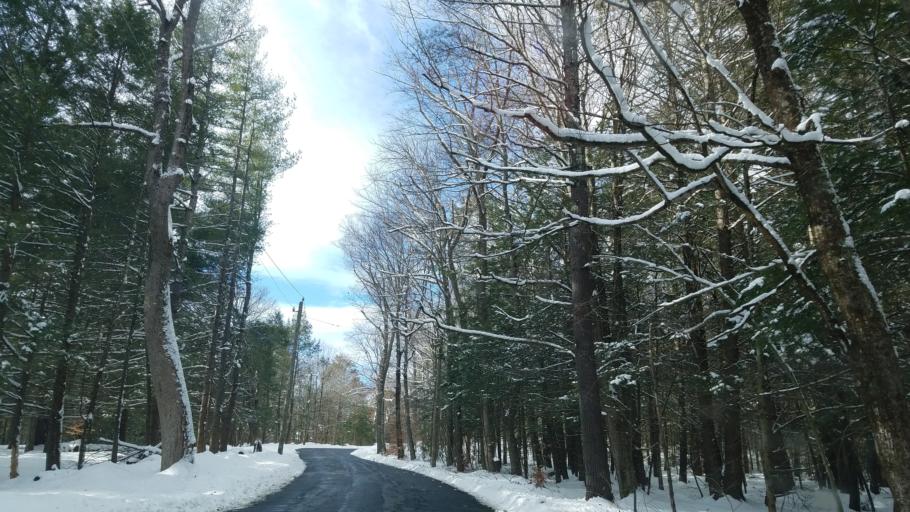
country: US
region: Connecticut
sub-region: Litchfield County
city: Winsted
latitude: 41.9676
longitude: -73.0540
